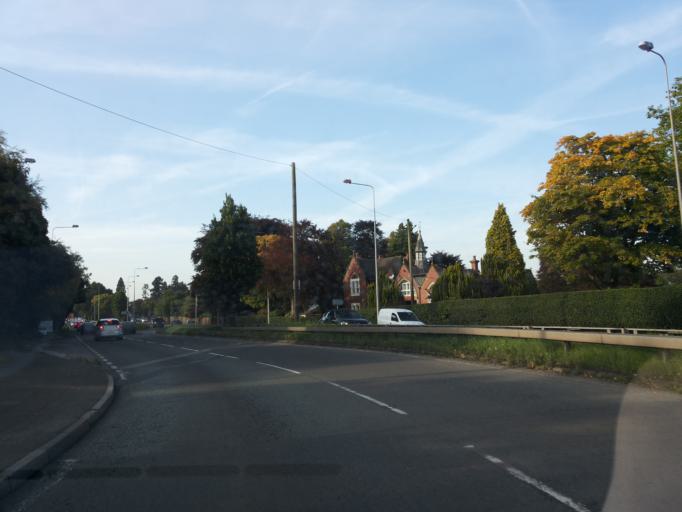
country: GB
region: England
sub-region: Staffordshire
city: Stone
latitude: 52.8869
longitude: -2.1367
